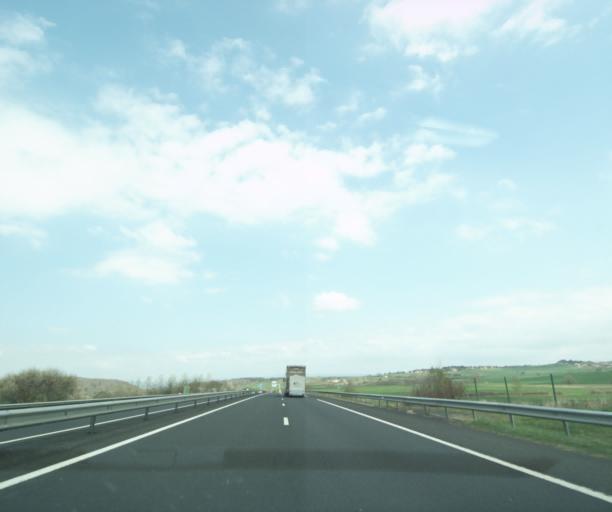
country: FR
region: Auvergne
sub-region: Departement du Cantal
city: Massiac
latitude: 45.2935
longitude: 3.2380
